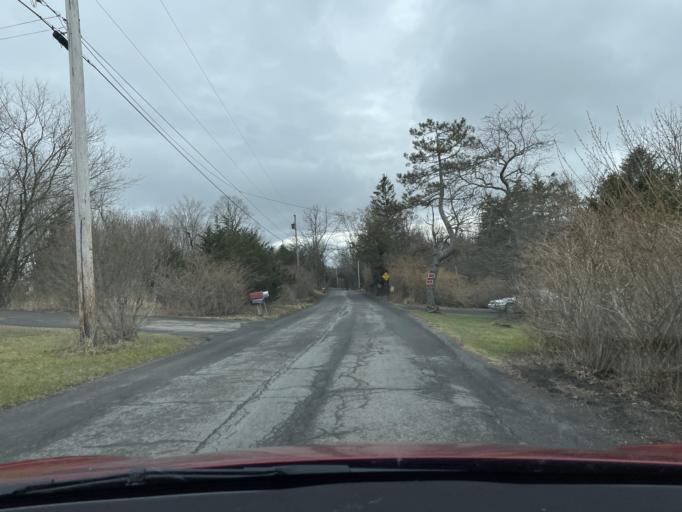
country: US
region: New York
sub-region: Ulster County
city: Manorville
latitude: 42.1037
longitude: -74.0335
